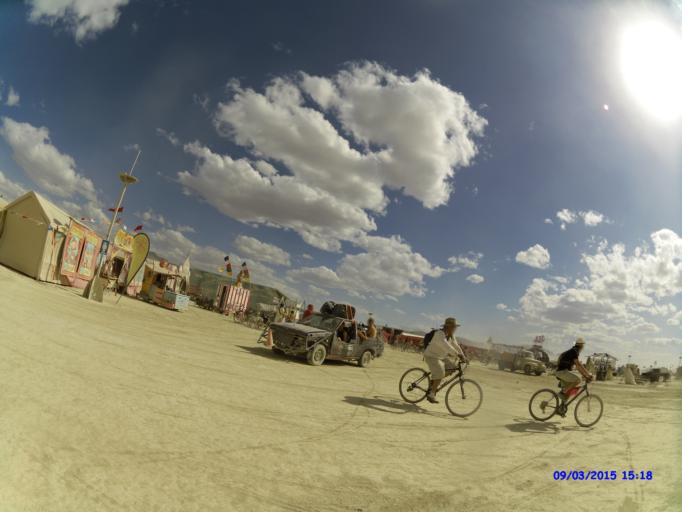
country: US
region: Nevada
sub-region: Pershing County
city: Lovelock
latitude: 40.7805
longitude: -119.1981
